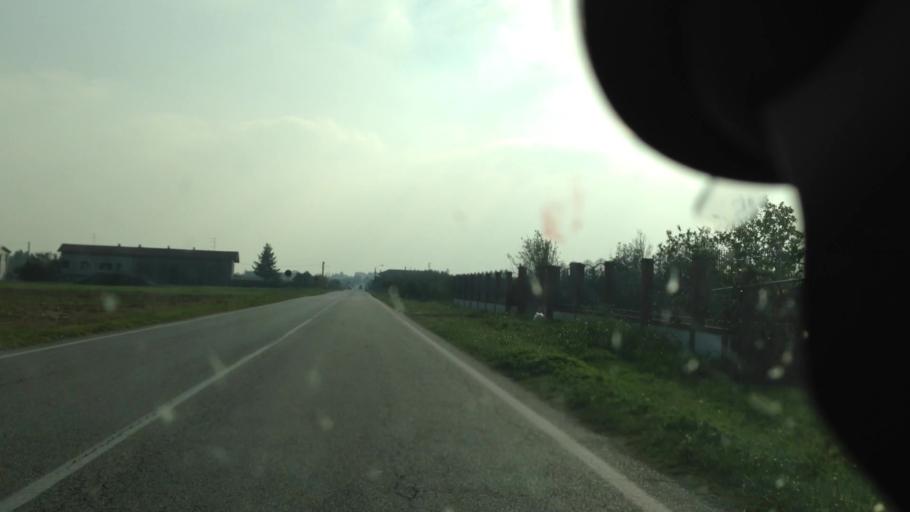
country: IT
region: Piedmont
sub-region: Provincia di Vercelli
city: Cigliano
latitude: 45.3269
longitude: 8.0364
